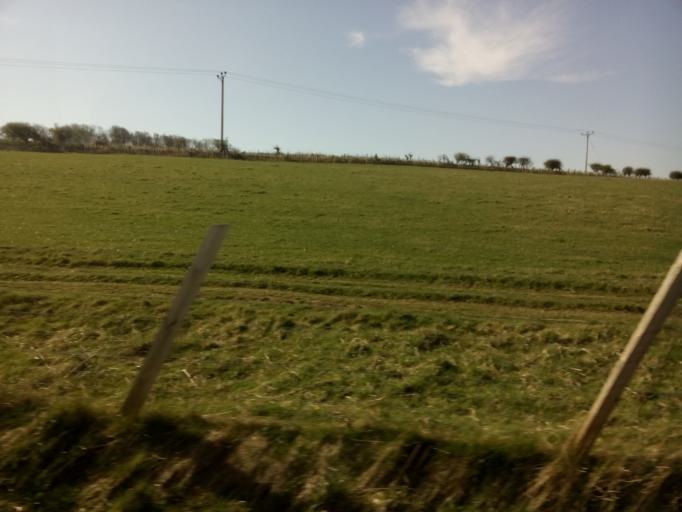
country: GB
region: Scotland
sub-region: The Scottish Borders
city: Eyemouth
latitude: 55.8334
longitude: -2.1444
